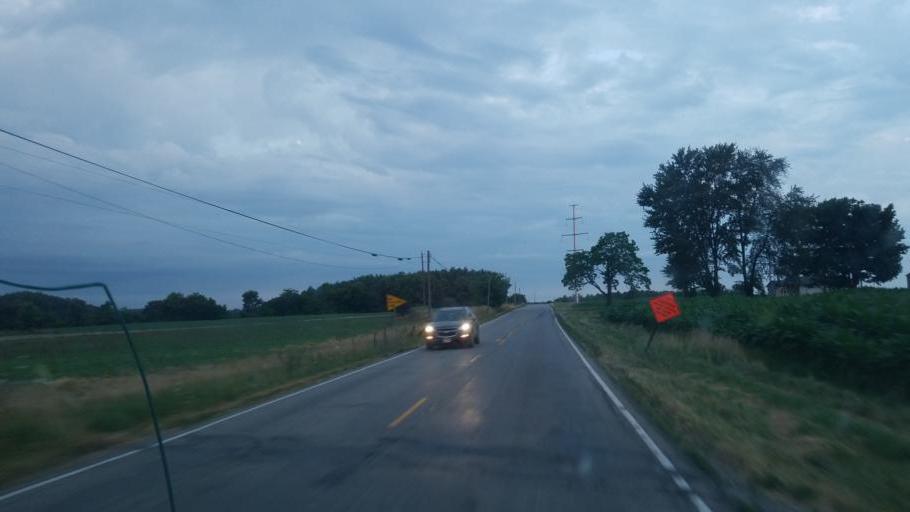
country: US
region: Ohio
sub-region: Defiance County
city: Hicksville
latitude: 41.3374
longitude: -84.8224
